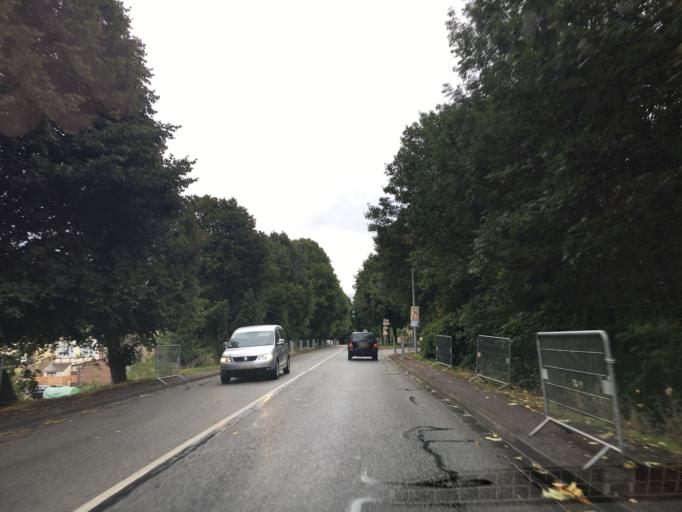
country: FR
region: Haute-Normandie
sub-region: Departement de l'Eure
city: Verneuil-sur-Avre
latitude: 48.7373
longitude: 0.9208
